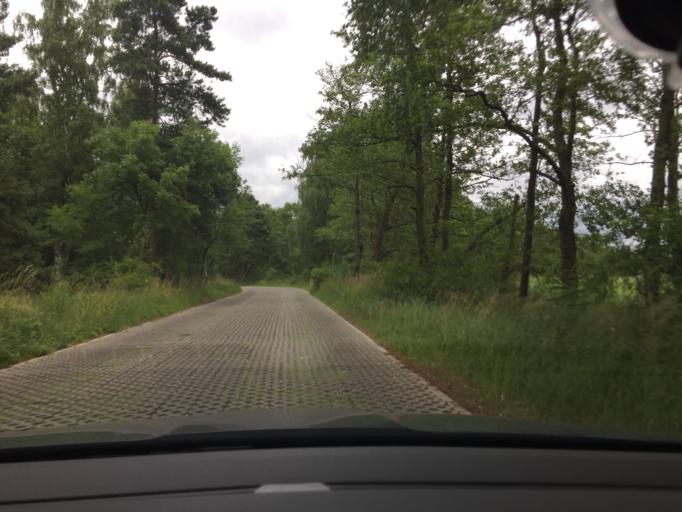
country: PL
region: Pomeranian Voivodeship
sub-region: Gdansk
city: Gdansk
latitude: 54.3643
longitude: 18.7711
